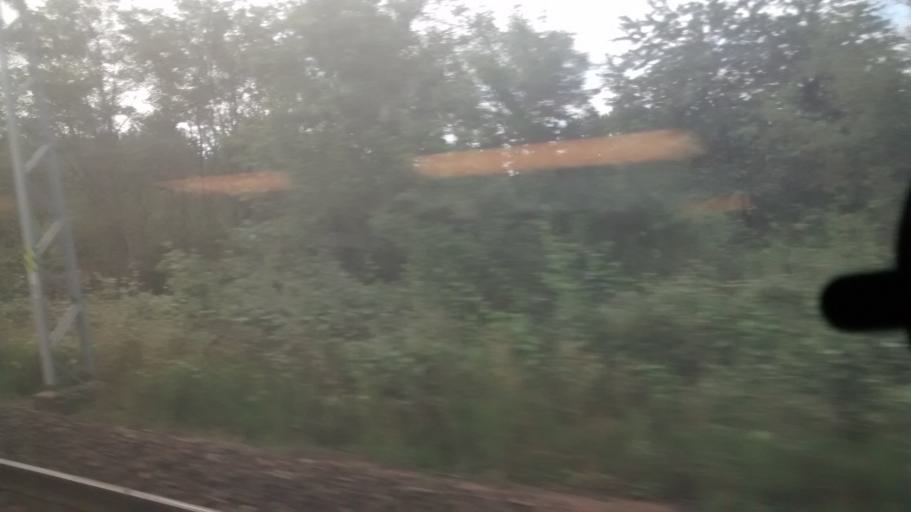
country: FR
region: Pays de la Loire
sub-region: Departement de la Sarthe
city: Change
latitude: 48.0076
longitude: 0.2751
